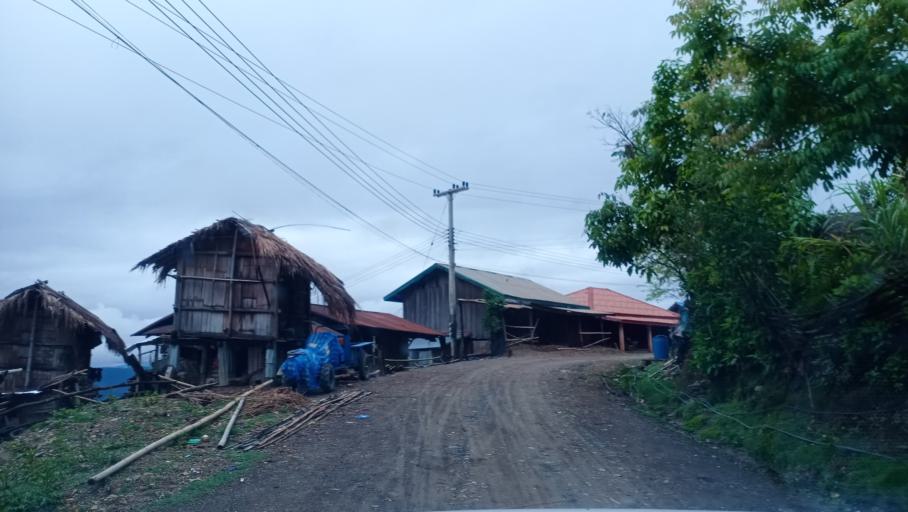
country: LA
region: Phongsali
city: Phongsali
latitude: 21.4491
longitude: 102.1612
